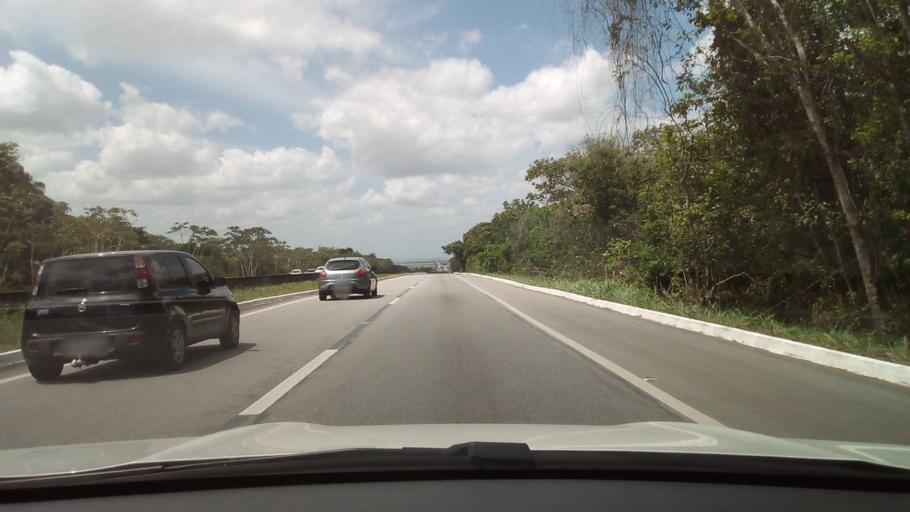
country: BR
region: Paraiba
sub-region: Mamanguape
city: Mamanguape
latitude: -6.9685
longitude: -35.0828
